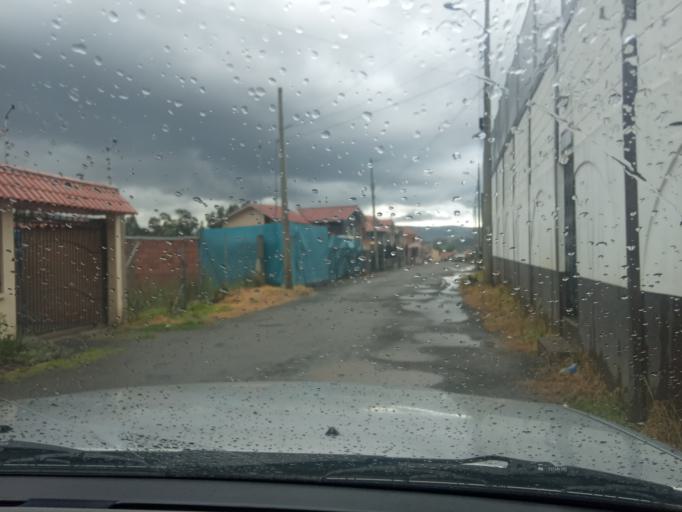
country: EC
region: Azuay
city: Llacao
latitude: -2.8662
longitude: -78.9437
